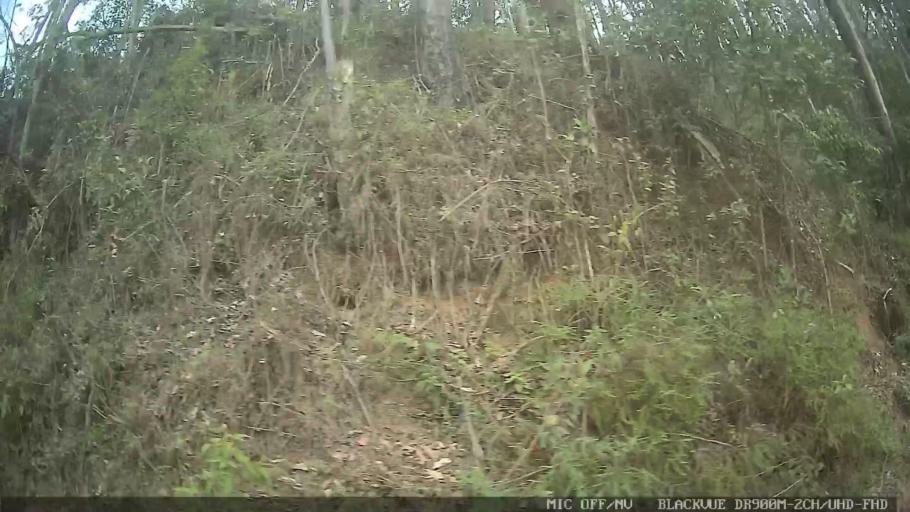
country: BR
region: Sao Paulo
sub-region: Bom Jesus Dos Perdoes
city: Bom Jesus dos Perdoes
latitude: -23.1735
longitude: -46.5152
